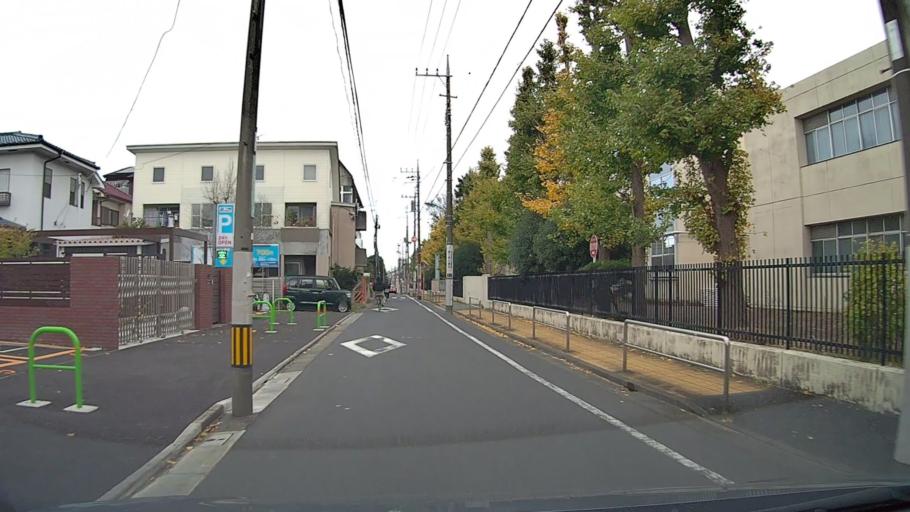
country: JP
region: Saitama
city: Wako
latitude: 35.7386
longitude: 139.6259
